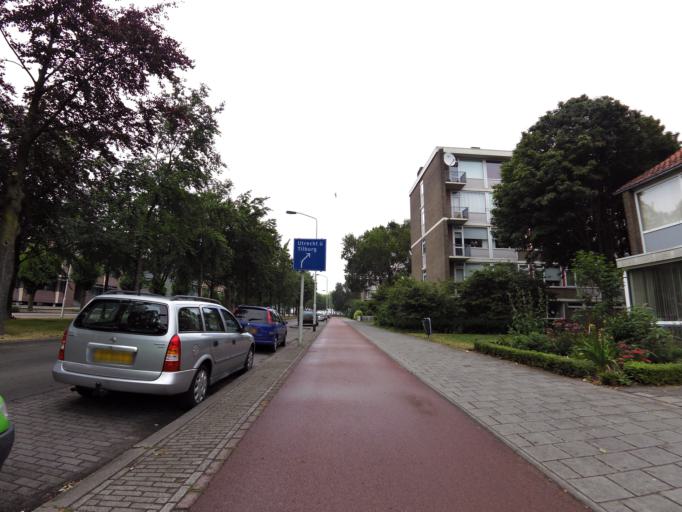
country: NL
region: North Brabant
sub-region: Gemeente Breda
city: Hoge Vucht
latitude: 51.5921
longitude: 4.8032
